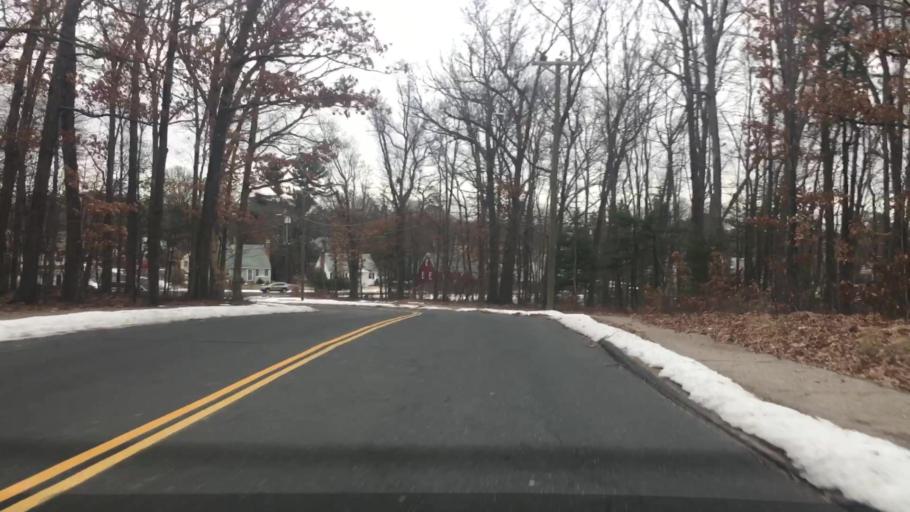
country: US
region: Connecticut
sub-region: Hartford County
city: Bristol
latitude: 41.6878
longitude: -72.9193
